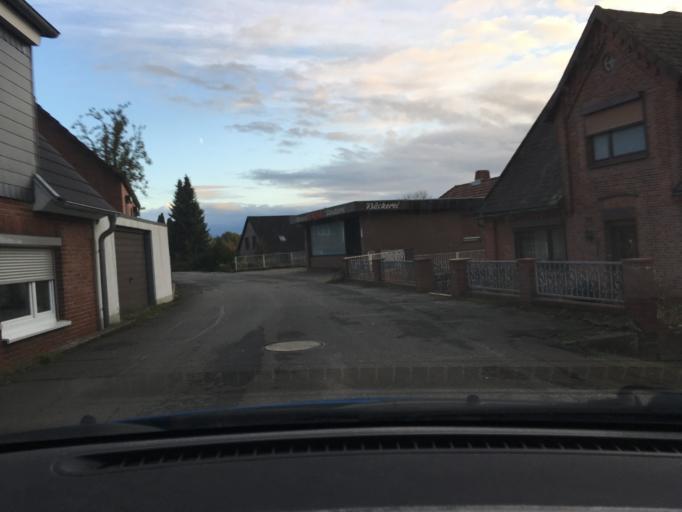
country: DE
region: Lower Saxony
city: Stelle
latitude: 53.4384
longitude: 10.0929
